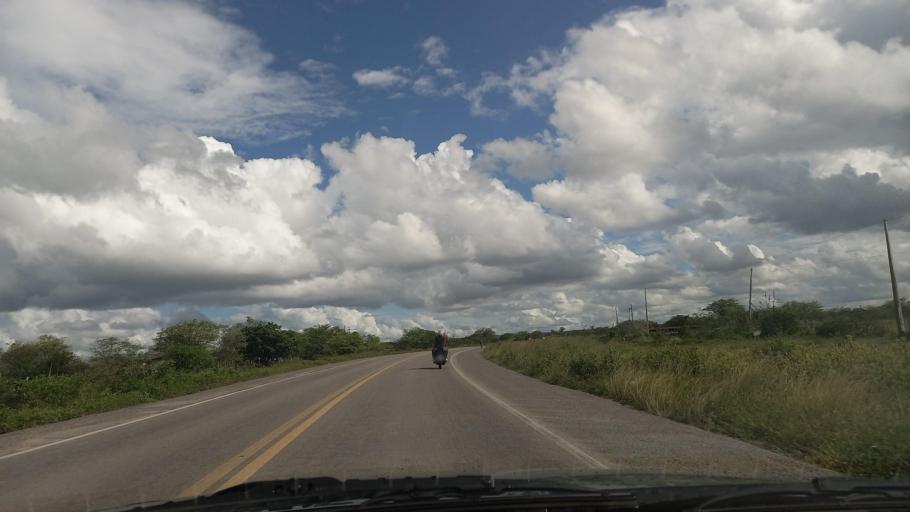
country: BR
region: Pernambuco
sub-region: Lajedo
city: Lajedo
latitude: -8.6081
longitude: -36.2941
